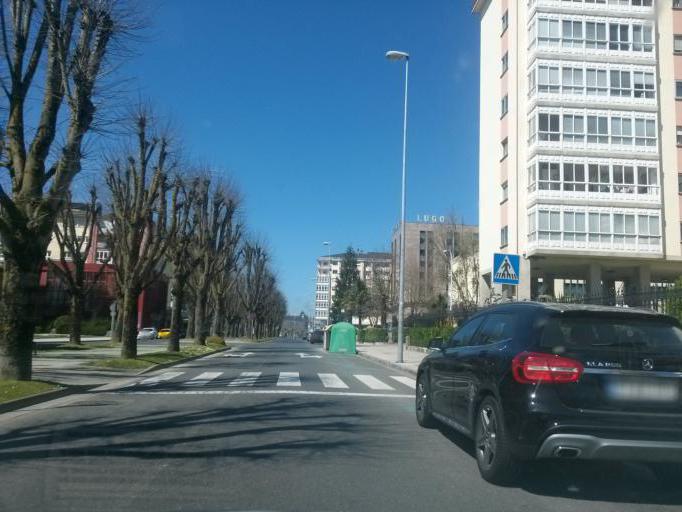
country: ES
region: Galicia
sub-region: Provincia de Lugo
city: Lugo
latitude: 43.0038
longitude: -7.5533
